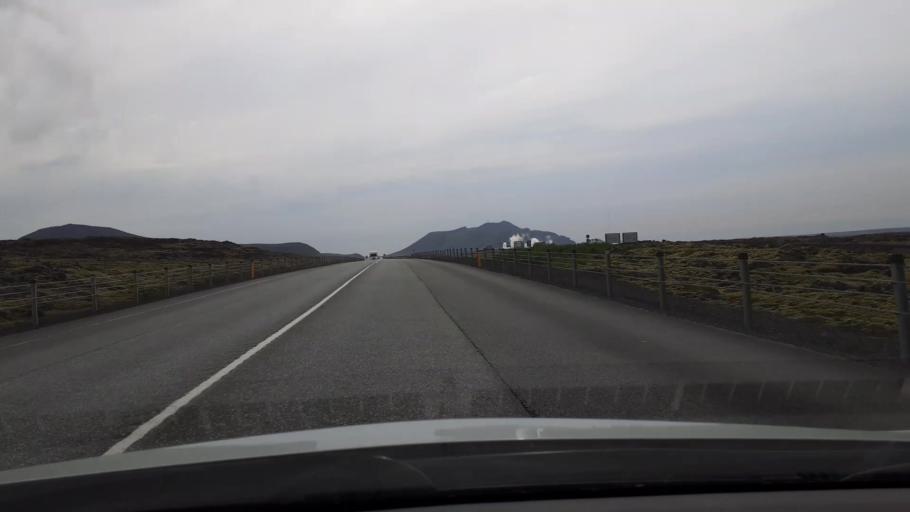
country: IS
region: Southern Peninsula
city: Grindavik
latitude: 63.9044
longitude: -22.4210
